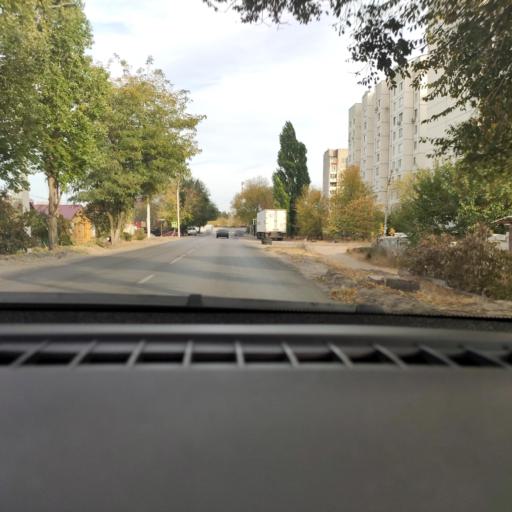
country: RU
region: Voronezj
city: Somovo
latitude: 51.7387
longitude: 39.2892
